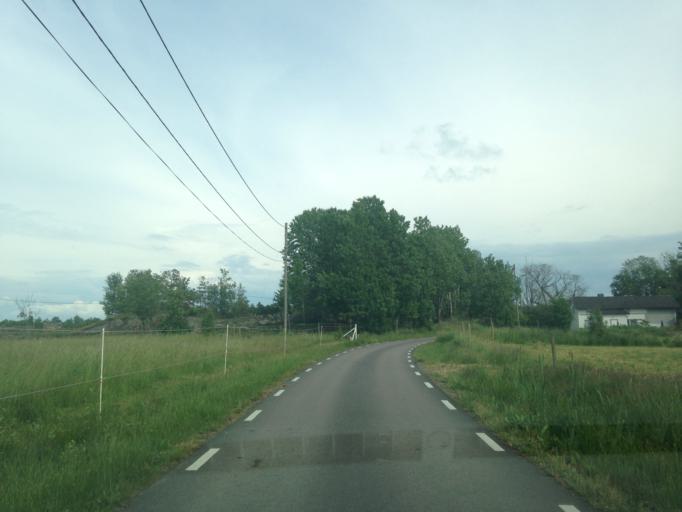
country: SE
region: Vaestra Goetaland
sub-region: Goteborg
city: Majorna
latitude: 57.7590
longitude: 11.8587
